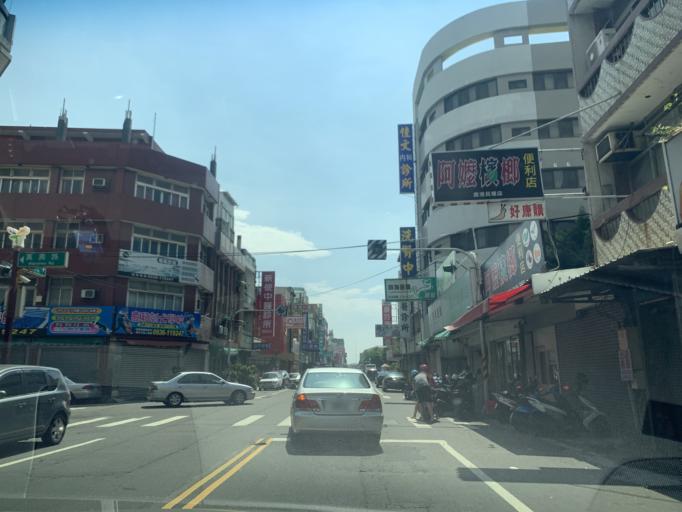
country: TW
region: Taiwan
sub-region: Changhua
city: Chang-hua
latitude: 24.0574
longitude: 120.4364
